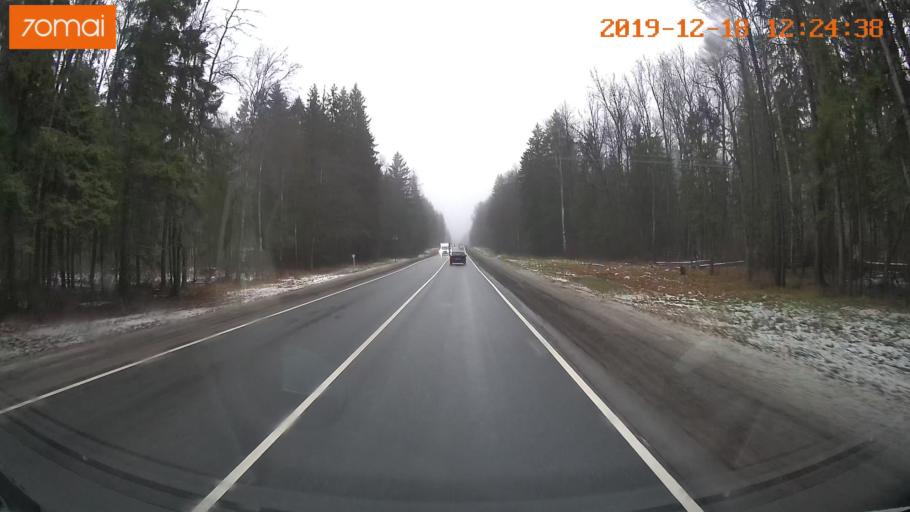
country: RU
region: Moskovskaya
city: Novopetrovskoye
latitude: 56.0271
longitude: 36.5009
